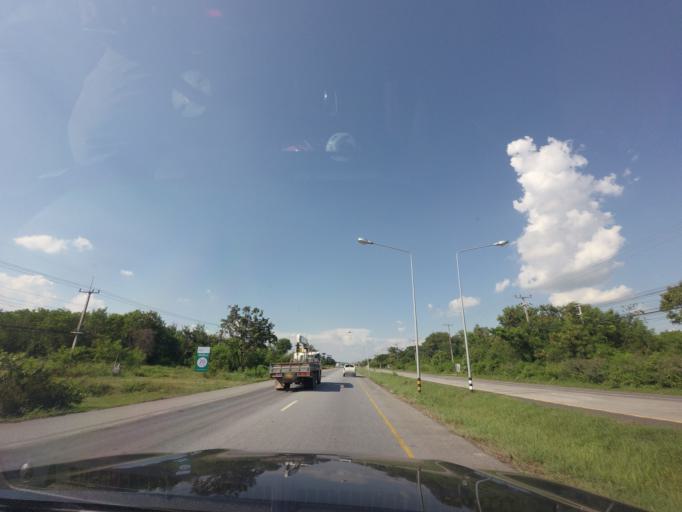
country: TH
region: Nakhon Ratchasima
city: Sida
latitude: 15.5402
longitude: 102.5462
